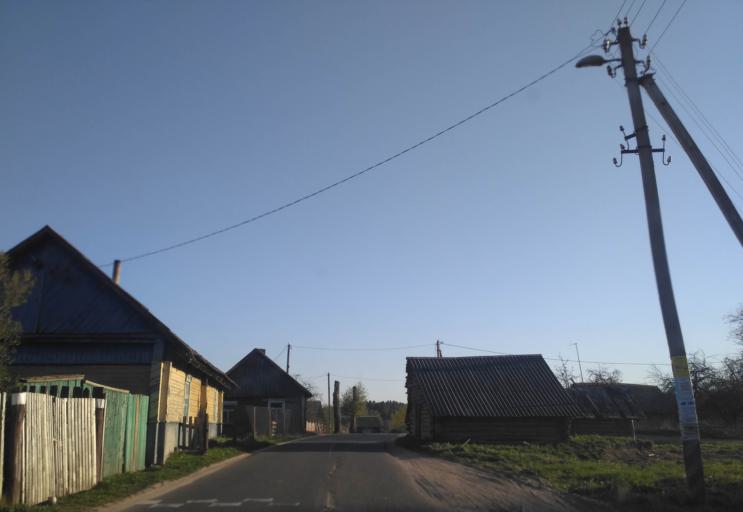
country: BY
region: Minsk
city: Radashkovichy
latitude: 54.1358
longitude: 27.2051
